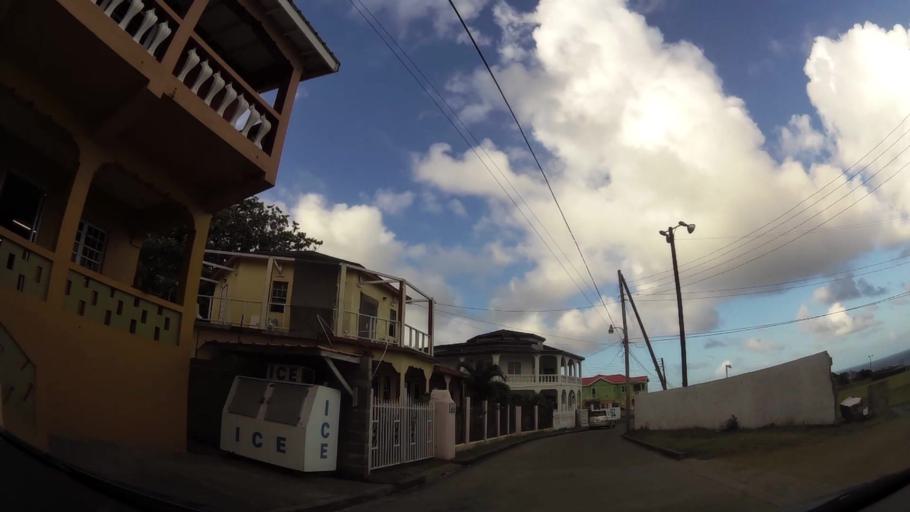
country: KN
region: Saint Mary Cayon
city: Cayon
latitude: 17.3492
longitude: -62.7284
